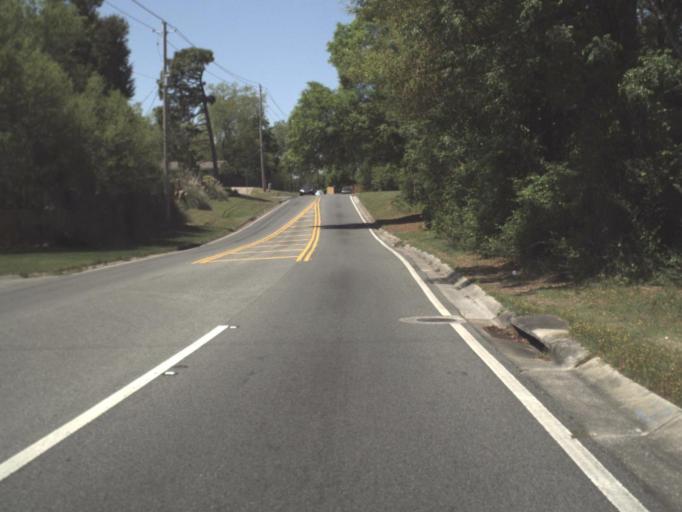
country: US
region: Florida
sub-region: Escambia County
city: Brent
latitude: 30.4949
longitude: -87.2379
